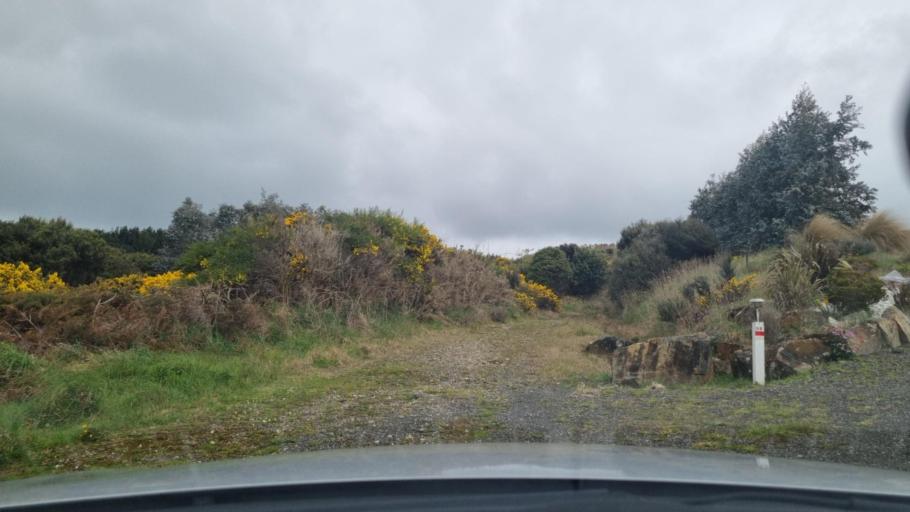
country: NZ
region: Southland
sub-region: Invercargill City
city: Bluff
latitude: -46.5772
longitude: 168.2978
